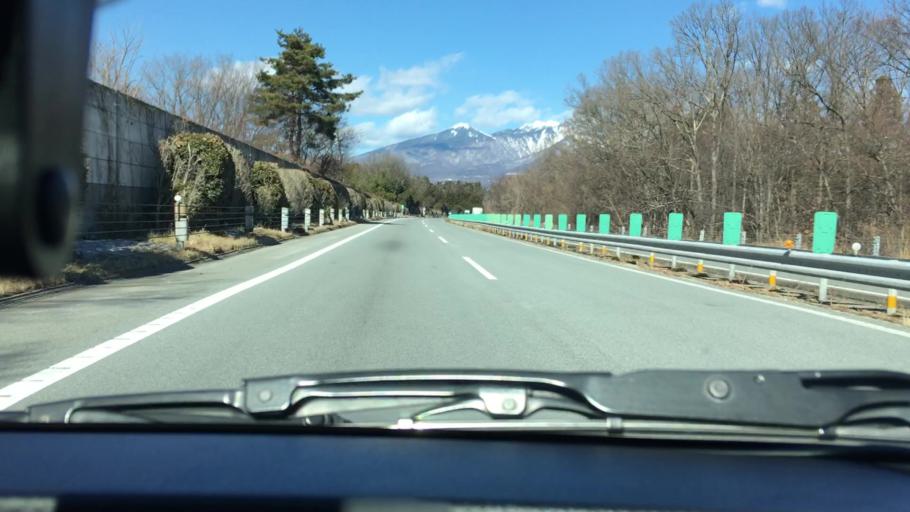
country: JP
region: Yamanashi
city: Nirasaki
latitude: 35.8115
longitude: 138.3947
